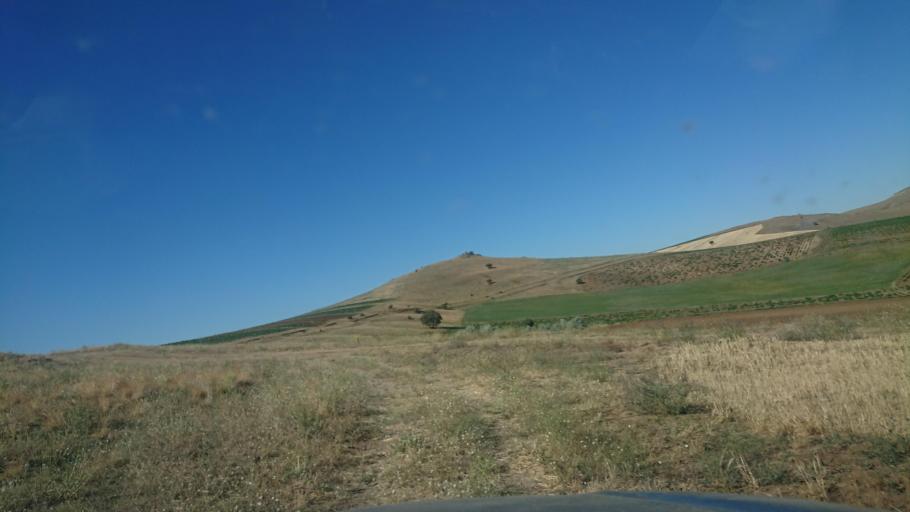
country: TR
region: Aksaray
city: Agacoren
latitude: 38.8383
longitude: 33.9363
